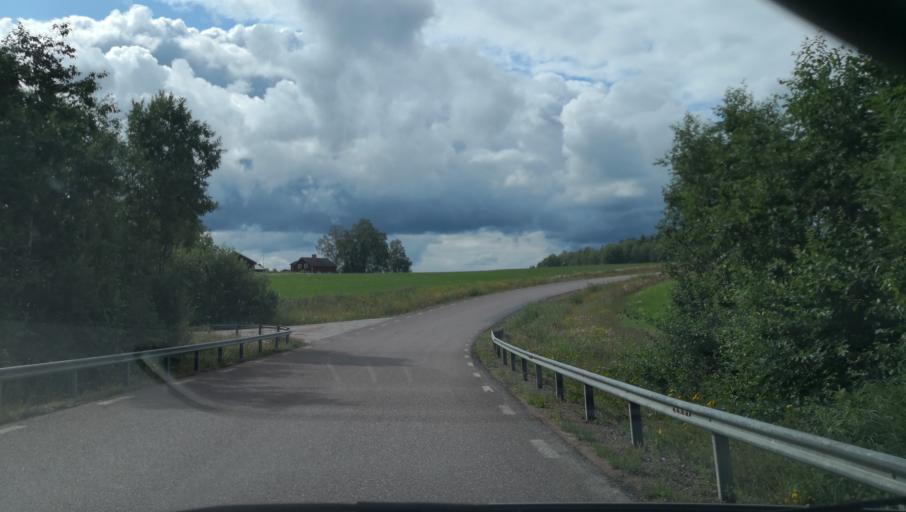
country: SE
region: Dalarna
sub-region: Borlange Kommun
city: Ornas
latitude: 60.4276
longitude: 15.6104
